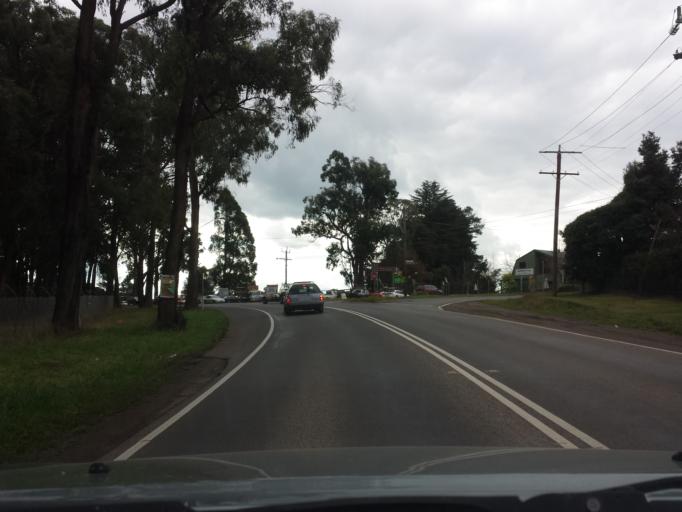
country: AU
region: Victoria
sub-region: Yarra Ranges
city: Monbulk
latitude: -37.8329
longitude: 145.4295
